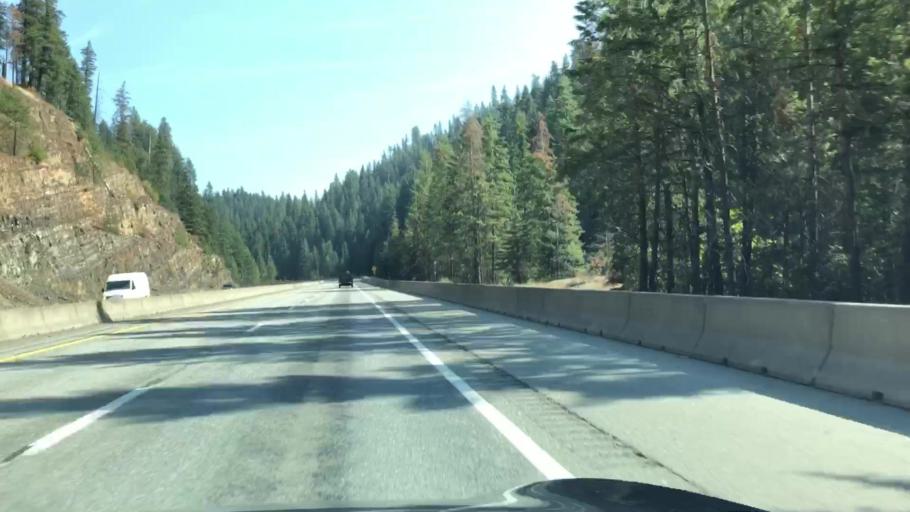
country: US
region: Idaho
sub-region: Kootenai County
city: Coeur d'Alene
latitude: 47.6242
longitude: -116.5851
